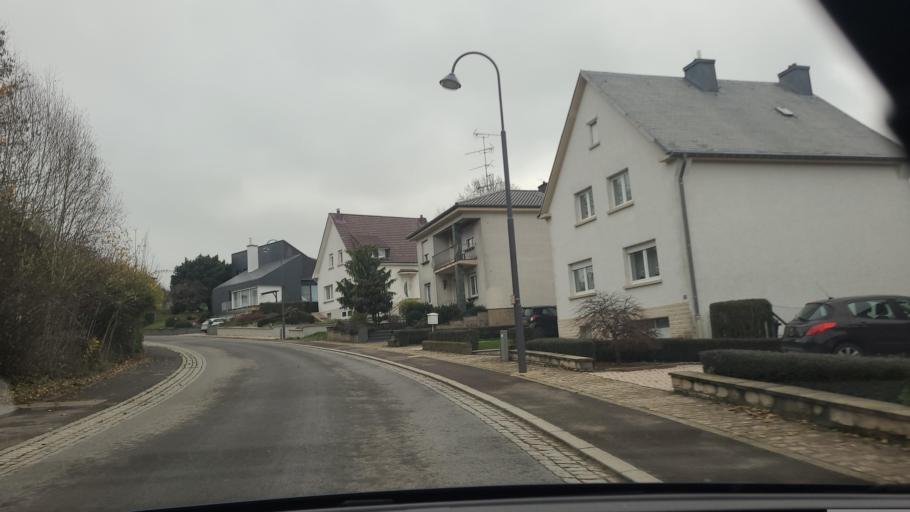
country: LU
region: Luxembourg
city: Schouweiler
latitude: 49.5836
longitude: 5.9568
